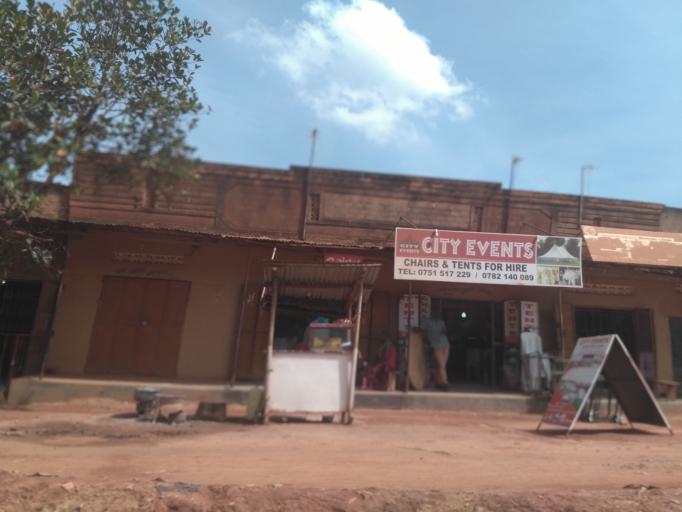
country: UG
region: Central Region
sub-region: Wakiso District
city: Kireka
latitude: 0.4398
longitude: 32.5996
